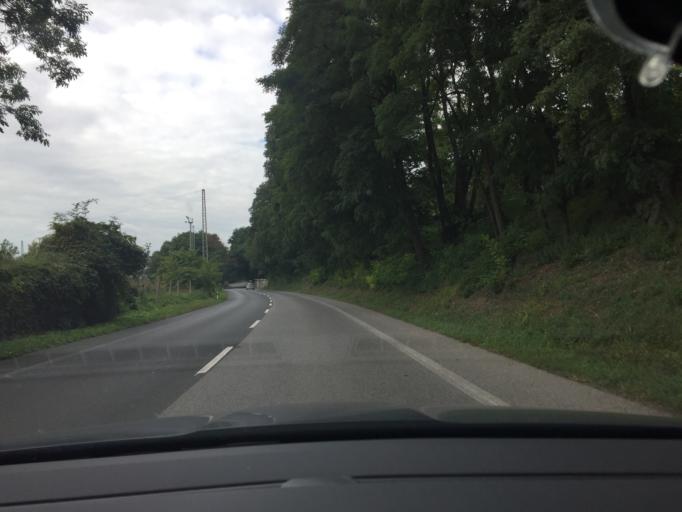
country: CZ
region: Ustecky
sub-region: Okres Litomerice
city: Litomerice
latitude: 50.5332
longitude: 14.1527
